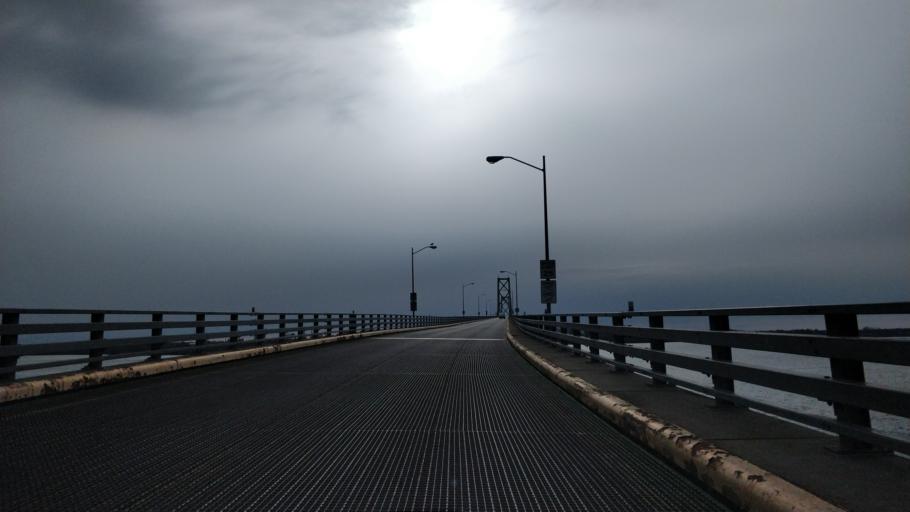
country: US
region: New York
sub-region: St. Lawrence County
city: Ogdensburg
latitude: 44.7427
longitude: -75.4653
